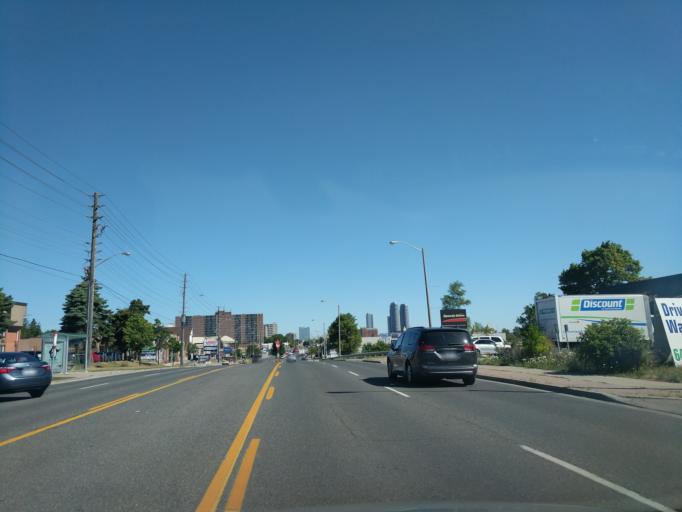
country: CA
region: Ontario
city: Scarborough
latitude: 43.7625
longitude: -79.2798
